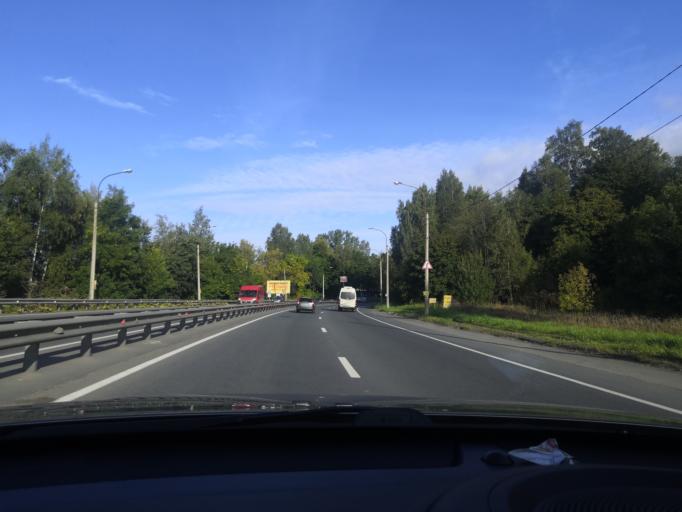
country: RU
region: St.-Petersburg
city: Pargolovo
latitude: 60.0795
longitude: 30.2655
